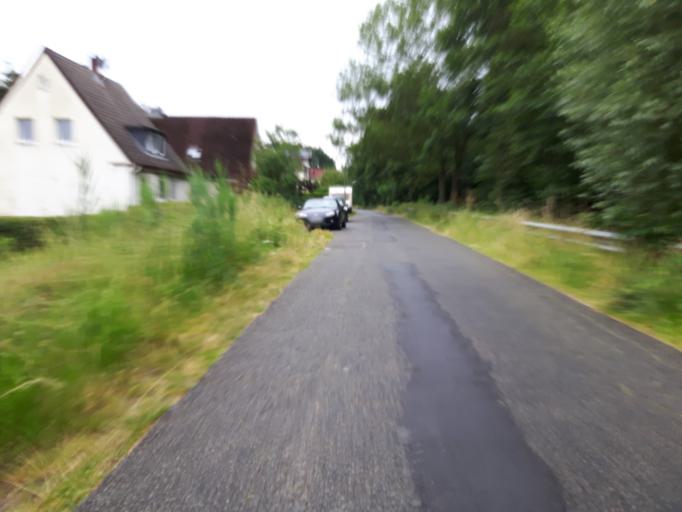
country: DE
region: Hamburg
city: Harburg
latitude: 53.4393
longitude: 10.0132
